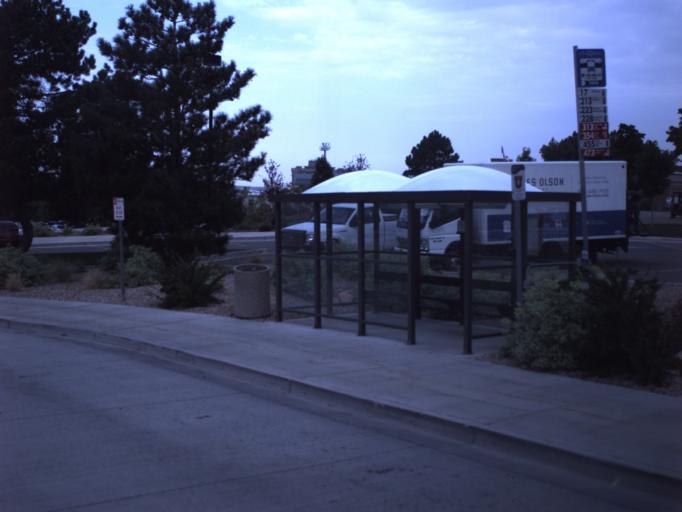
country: US
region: Utah
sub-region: Salt Lake County
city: Salt Lake City
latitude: 40.7612
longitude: -111.8380
